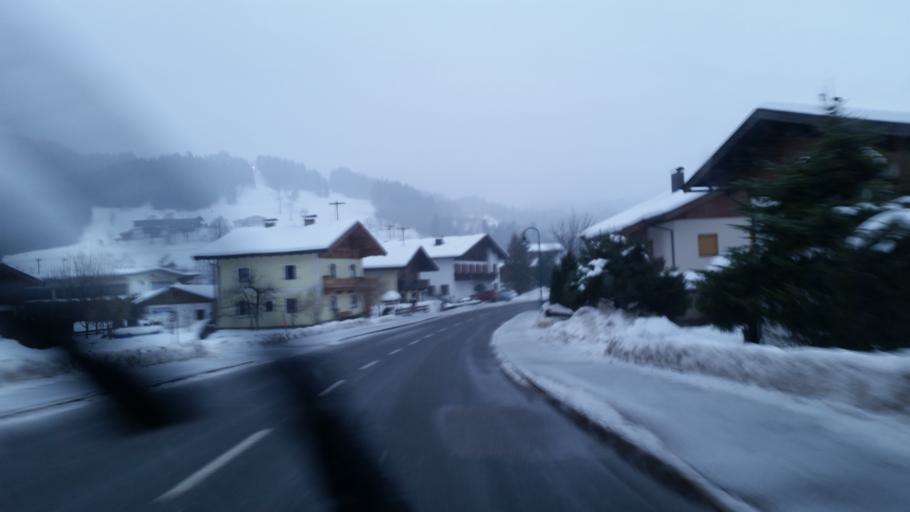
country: AT
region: Tyrol
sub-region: Politischer Bezirk Kitzbuhel
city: Kirchdorf in Tirol
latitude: 47.5561
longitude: 12.4504
